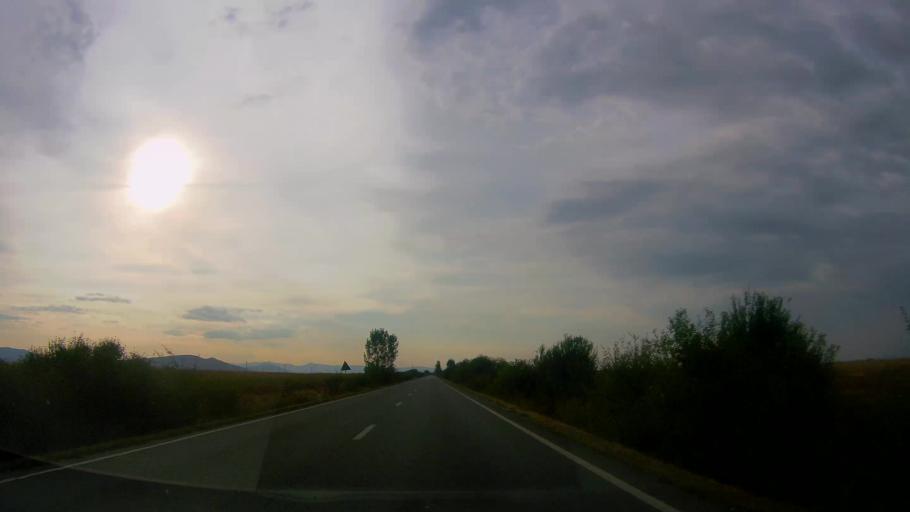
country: RO
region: Satu Mare
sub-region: Comuna Turulung
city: Turulung
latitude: 47.9542
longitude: 23.0608
